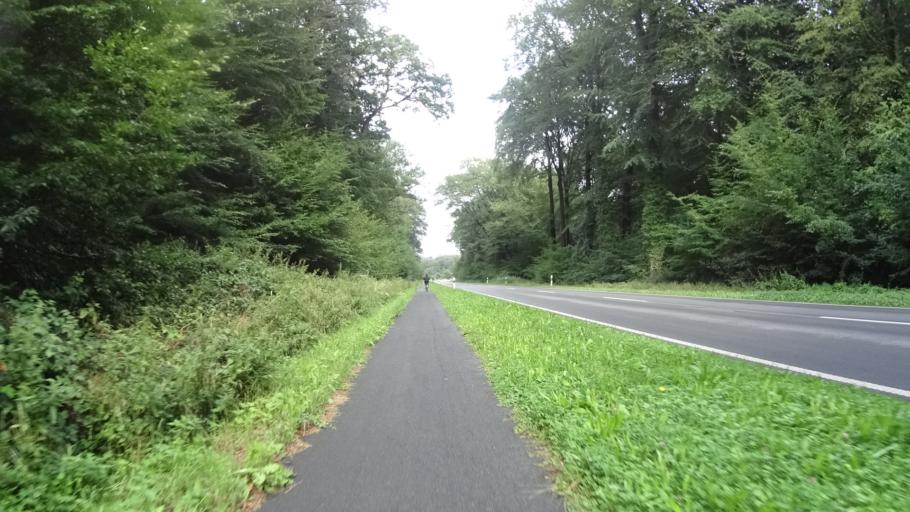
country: DE
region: Lower Saxony
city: Zetel
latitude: 53.3931
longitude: 7.9683
